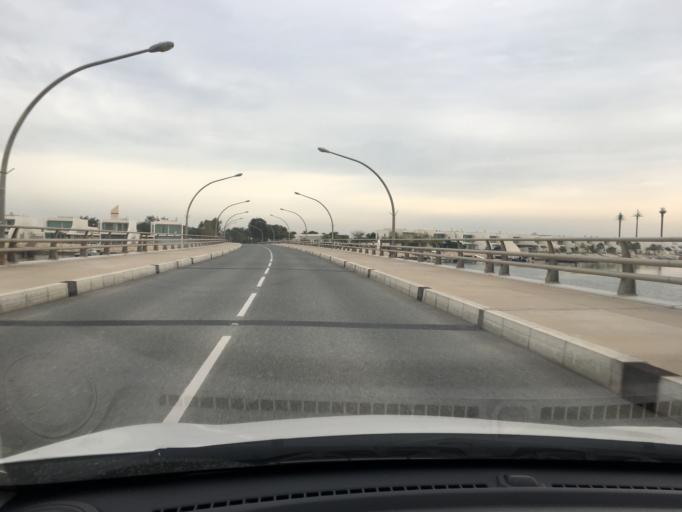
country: BH
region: Central Governorate
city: Dar Kulayb
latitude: 25.8312
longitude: 50.6123
